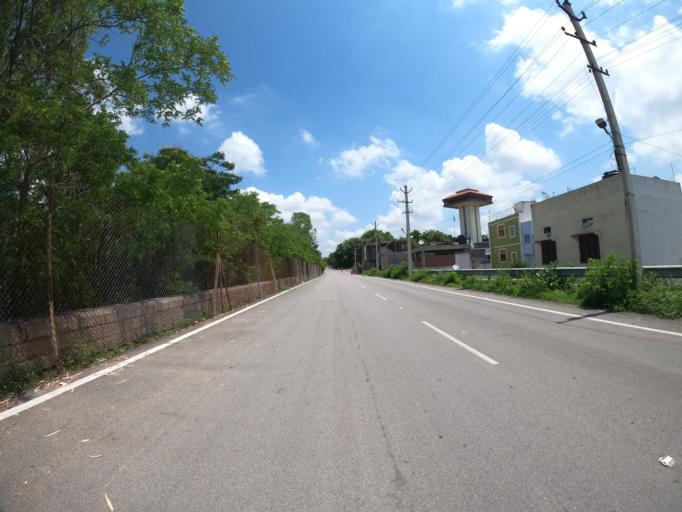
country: IN
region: Telangana
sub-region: Medak
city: Serilingampalle
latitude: 17.3874
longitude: 78.3162
